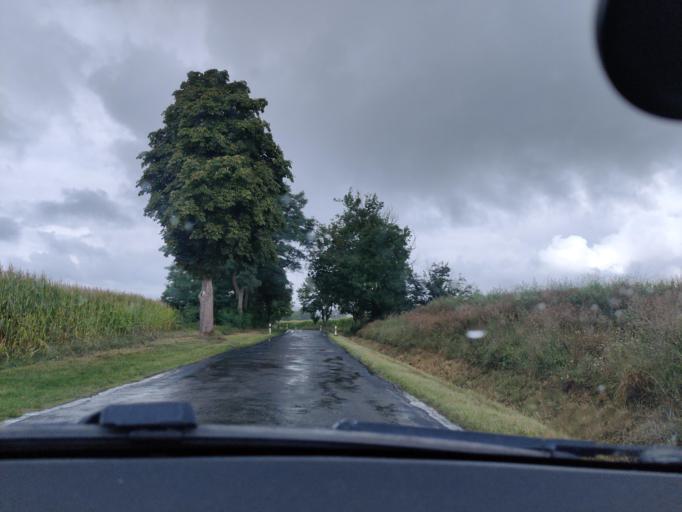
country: DE
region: Mecklenburg-Vorpommern
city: Wesenberg
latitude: 53.2708
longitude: 13.0007
